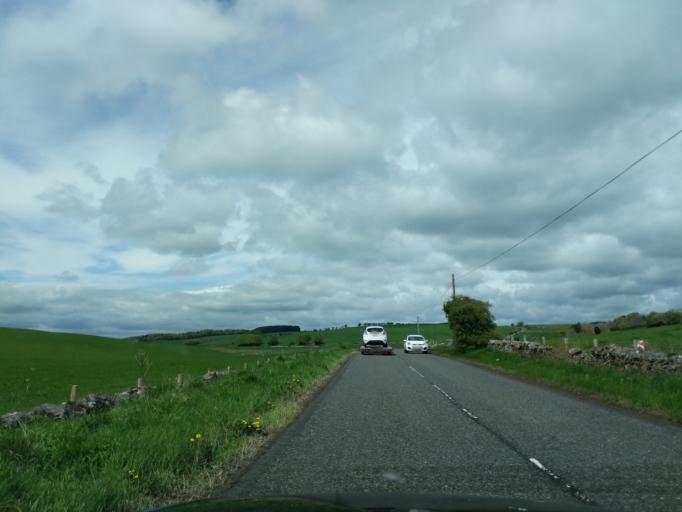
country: GB
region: Scotland
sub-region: The Scottish Borders
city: Earlston
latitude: 55.6974
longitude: -2.5905
